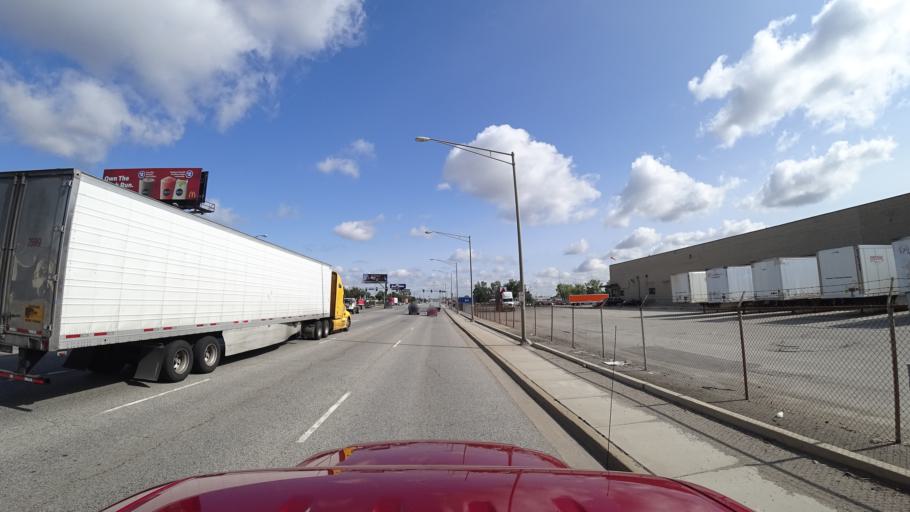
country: US
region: Illinois
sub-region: Cook County
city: Cicero
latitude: 41.8249
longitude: -87.7434
